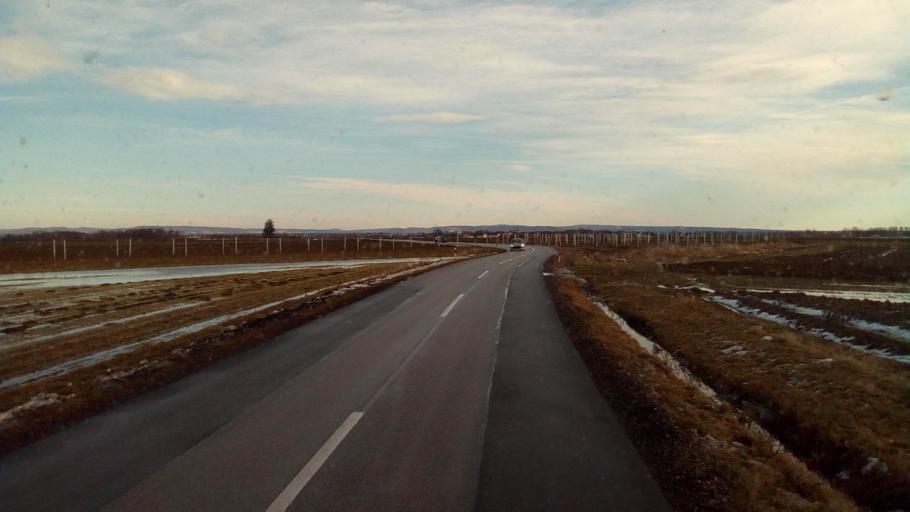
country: HR
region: Medimurska
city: Gardinovec
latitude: 46.4183
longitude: 16.5367
